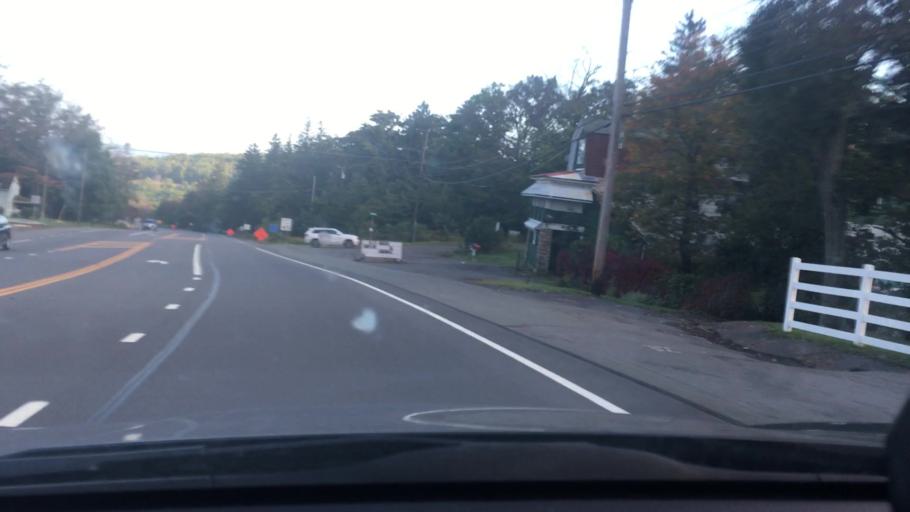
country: US
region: Pennsylvania
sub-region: Luzerne County
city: Hudson
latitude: 41.2327
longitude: -75.8013
